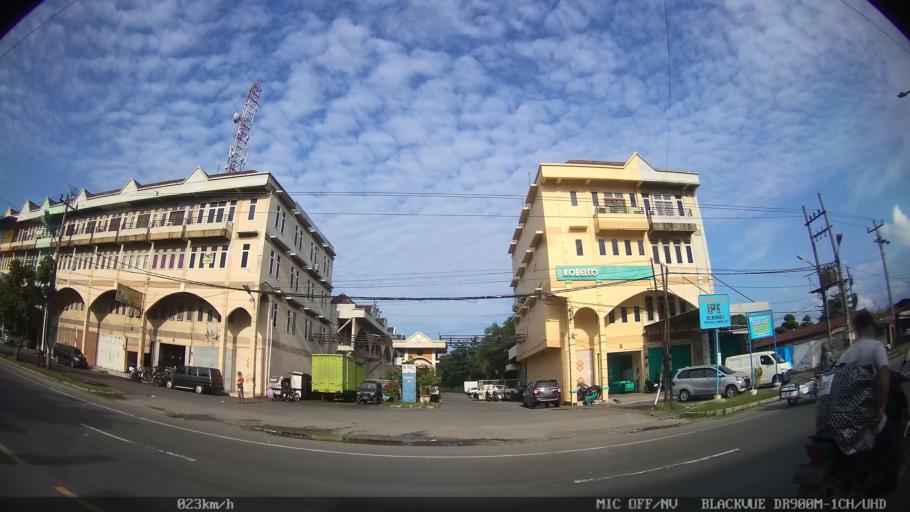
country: ID
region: North Sumatra
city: Medan
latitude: 3.6377
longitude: 98.6814
